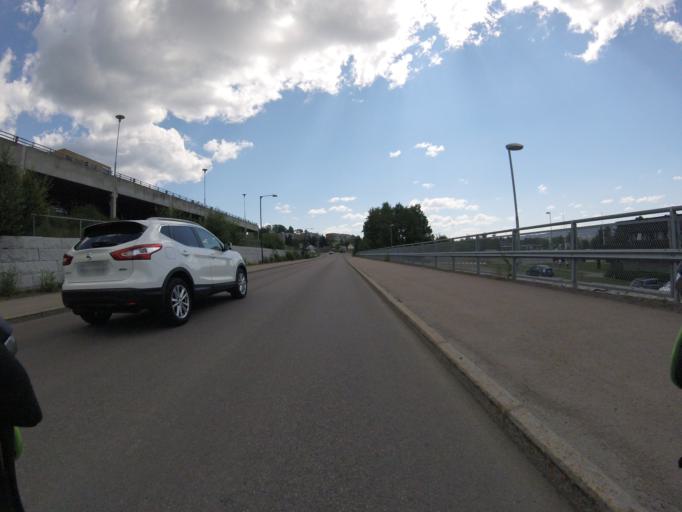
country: NO
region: Akershus
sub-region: Skedsmo
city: Lillestrom
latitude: 59.9717
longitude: 11.0502
